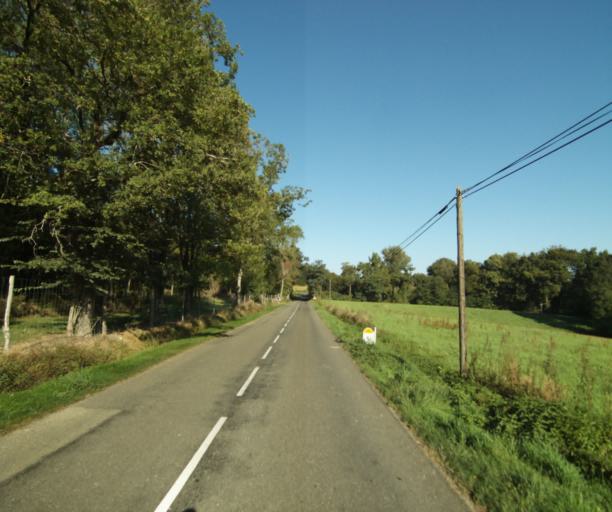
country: FR
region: Aquitaine
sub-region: Departement des Landes
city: Gabarret
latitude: 43.9273
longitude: 0.0179
